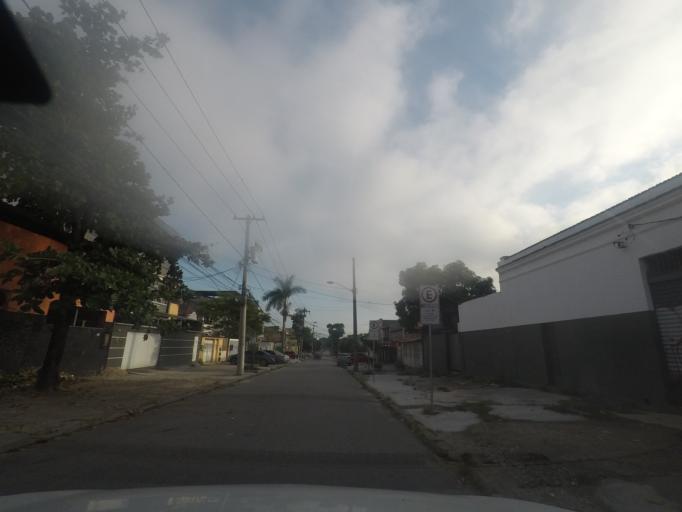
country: BR
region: Rio de Janeiro
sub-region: Duque De Caxias
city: Duque de Caxias
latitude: -22.8394
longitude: -43.2731
